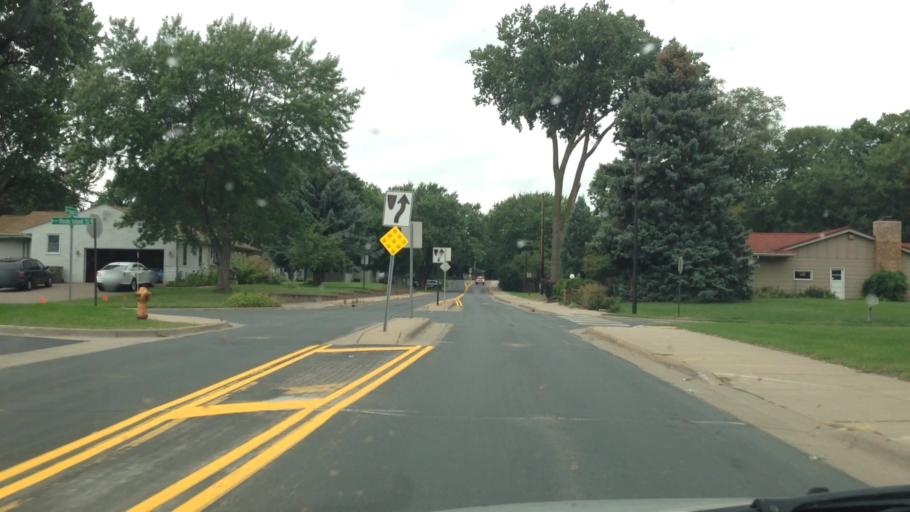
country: US
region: Minnesota
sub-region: Hennepin County
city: Saint Louis Park
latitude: 44.9747
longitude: -93.3777
